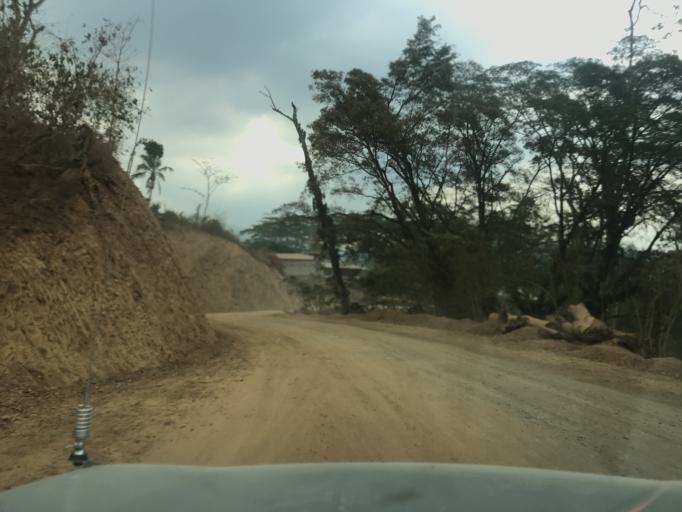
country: TL
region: Ermera
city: Gleno
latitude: -8.7604
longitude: 125.4309
